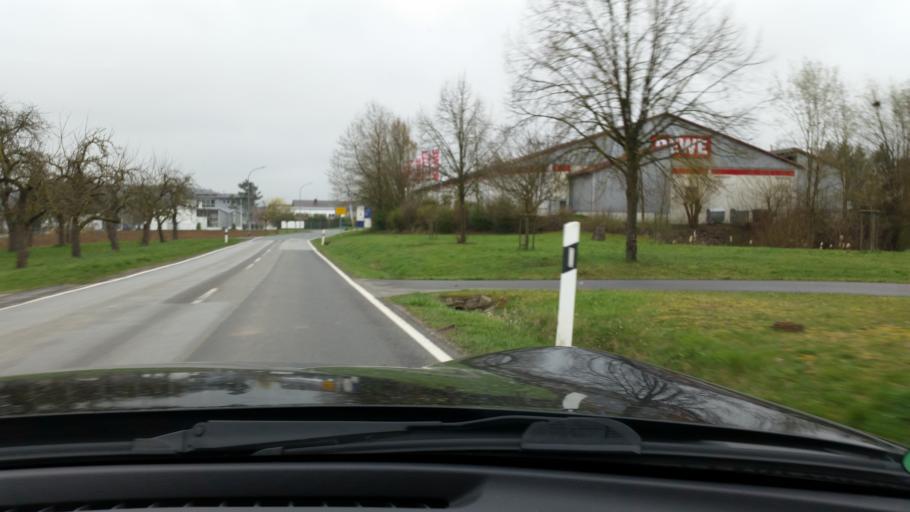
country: DE
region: Baden-Wuerttemberg
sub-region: Karlsruhe Region
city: Hardheim
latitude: 49.6189
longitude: 9.4756
